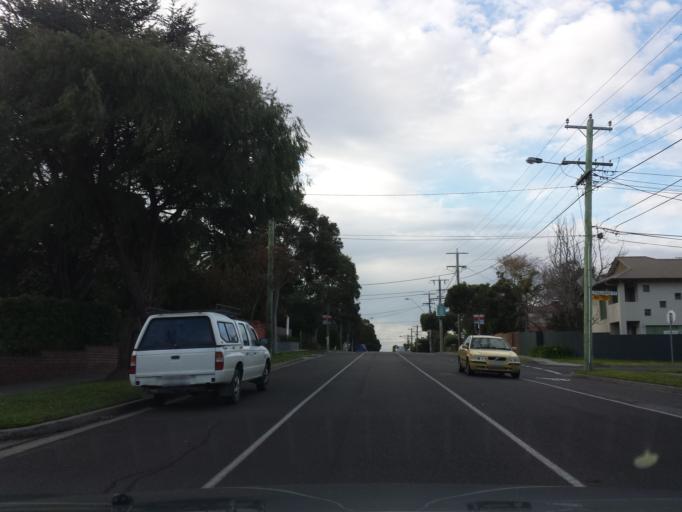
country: AU
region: Victoria
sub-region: Bayside
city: Cheltenham
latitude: -37.9723
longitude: 145.0544
